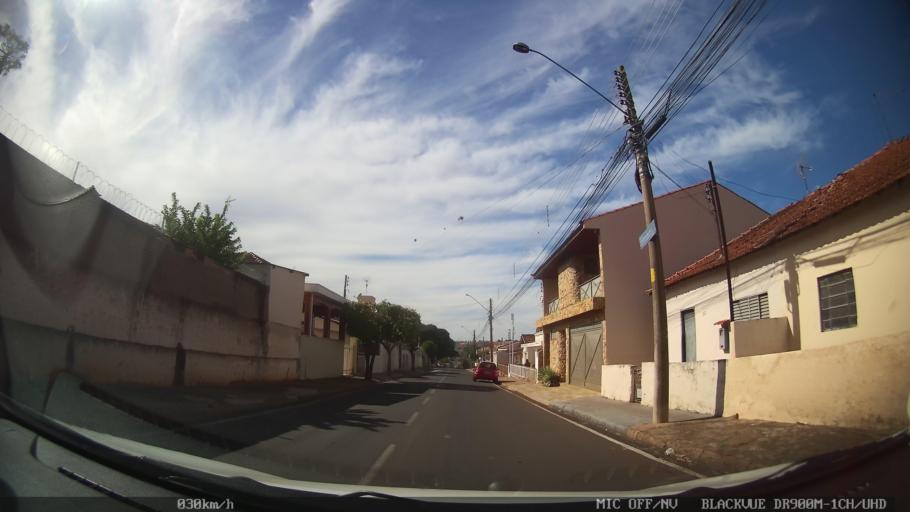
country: BR
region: Sao Paulo
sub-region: Catanduva
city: Catanduva
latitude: -21.1272
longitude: -48.9657
